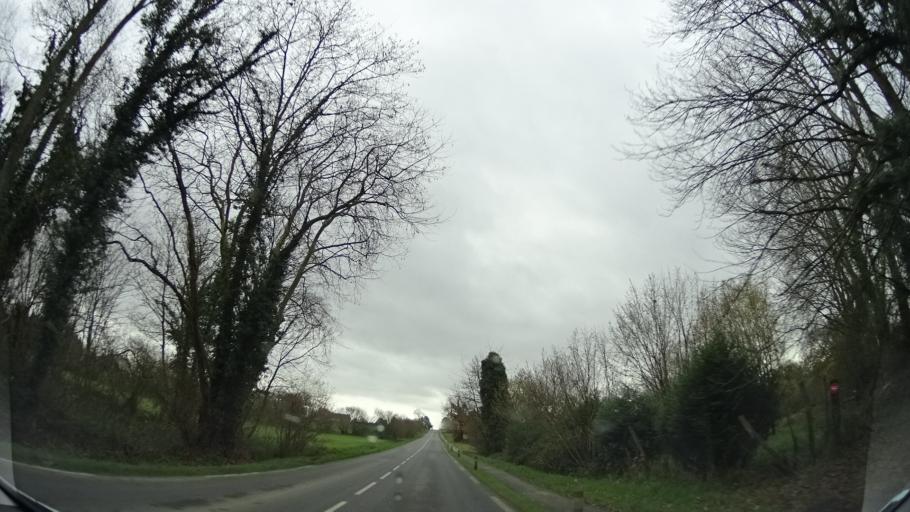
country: FR
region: Brittany
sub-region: Departement des Cotes-d'Armor
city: Lanvallay
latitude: 48.4439
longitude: -2.0198
